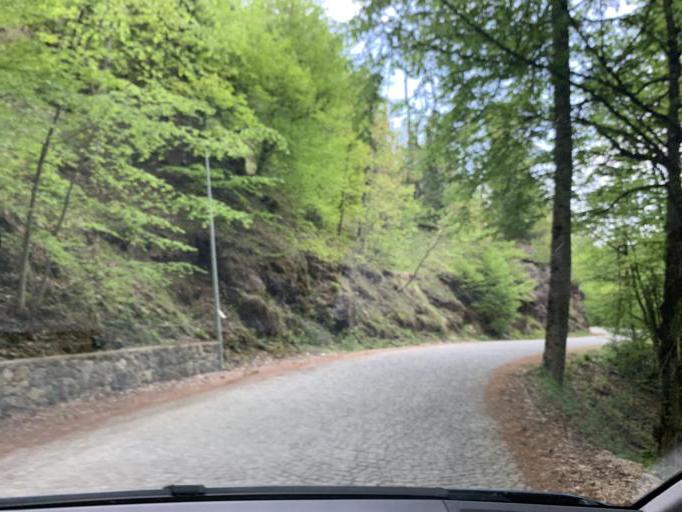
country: TR
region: Zonguldak
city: Egerci
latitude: 40.9368
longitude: 31.7407
